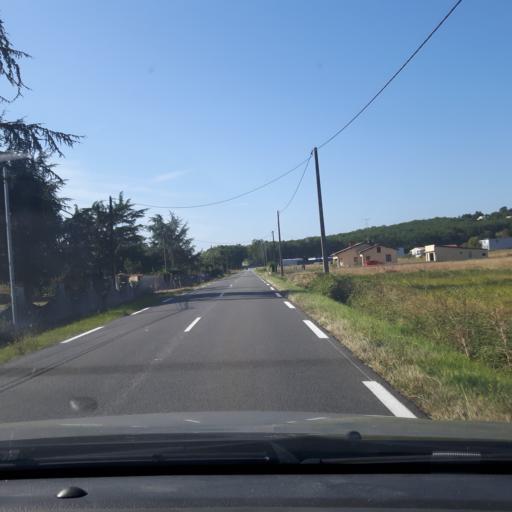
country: FR
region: Midi-Pyrenees
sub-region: Departement de la Haute-Garonne
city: Montjoire
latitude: 43.7740
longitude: 1.5500
